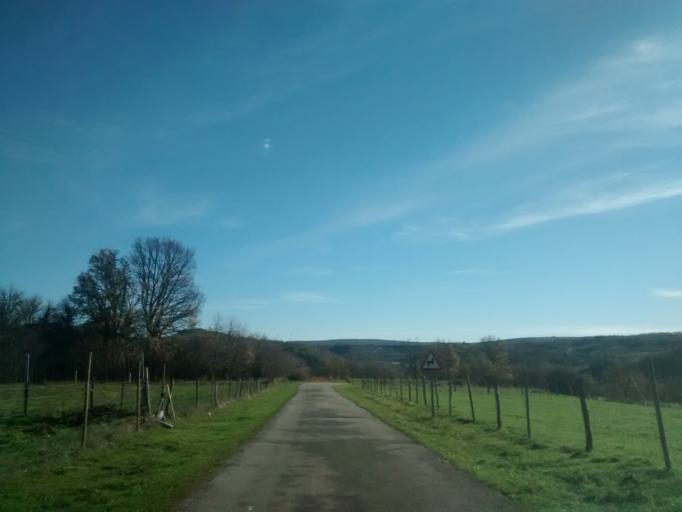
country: ES
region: Cantabria
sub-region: Provincia de Cantabria
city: San Pedro del Romeral
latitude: 42.9692
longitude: -3.7554
